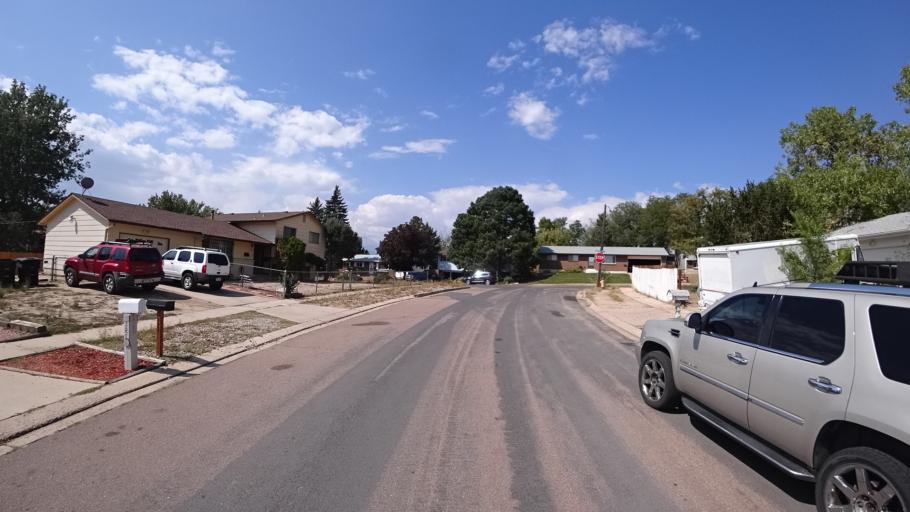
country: US
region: Colorado
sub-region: El Paso County
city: Stratmoor
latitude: 38.8277
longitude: -104.7648
